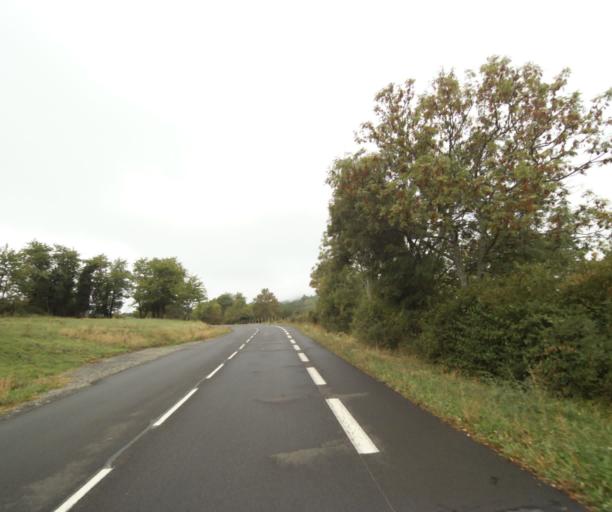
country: FR
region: Auvergne
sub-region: Departement du Puy-de-Dome
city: Romagnat
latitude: 45.7186
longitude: 3.0916
